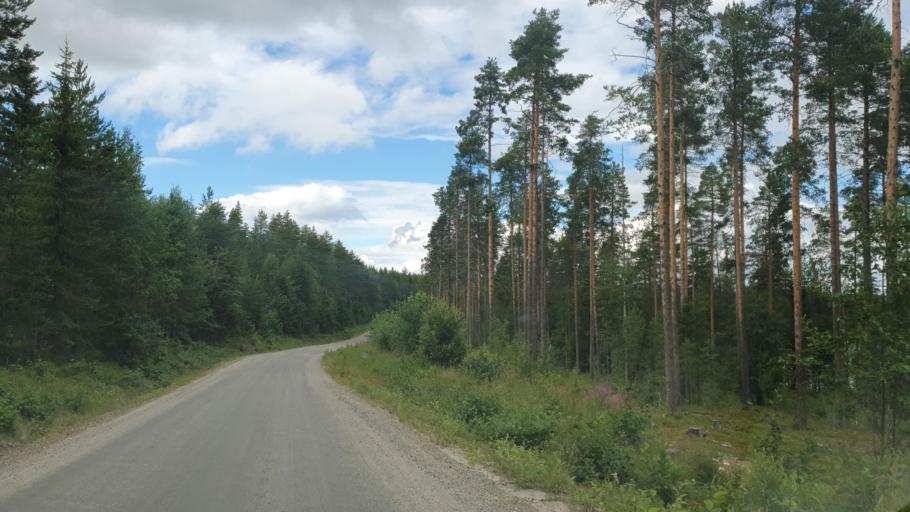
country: FI
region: Kainuu
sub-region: Kehys-Kainuu
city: Kuhmo
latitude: 64.0976
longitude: 29.4103
